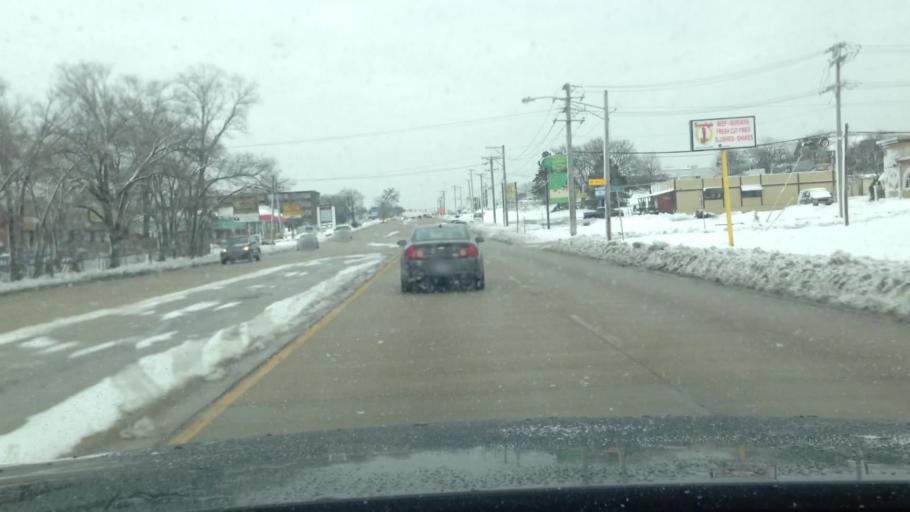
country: US
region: Illinois
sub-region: DuPage County
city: Lombard
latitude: 41.8596
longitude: -88.0352
